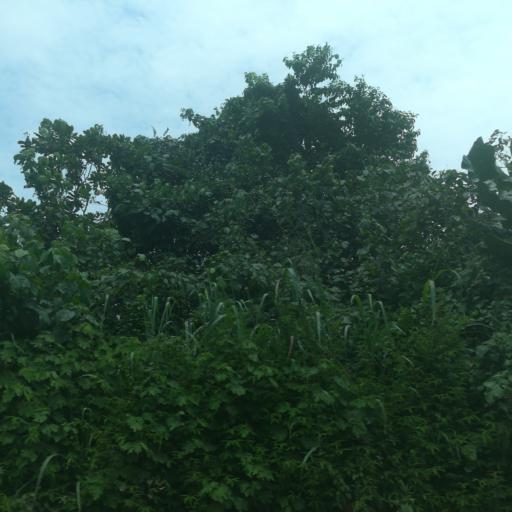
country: NG
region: Lagos
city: Ejirin
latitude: 6.6641
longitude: 3.7933
